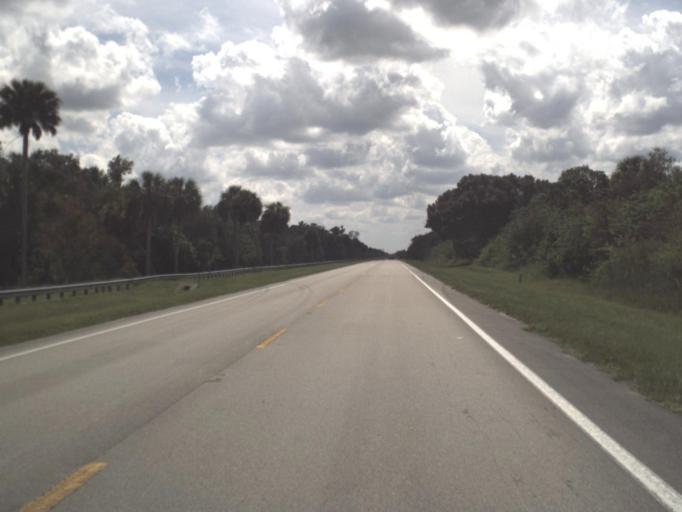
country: US
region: Florida
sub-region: Collier County
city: Orangetree
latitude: 26.1141
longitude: -81.3448
